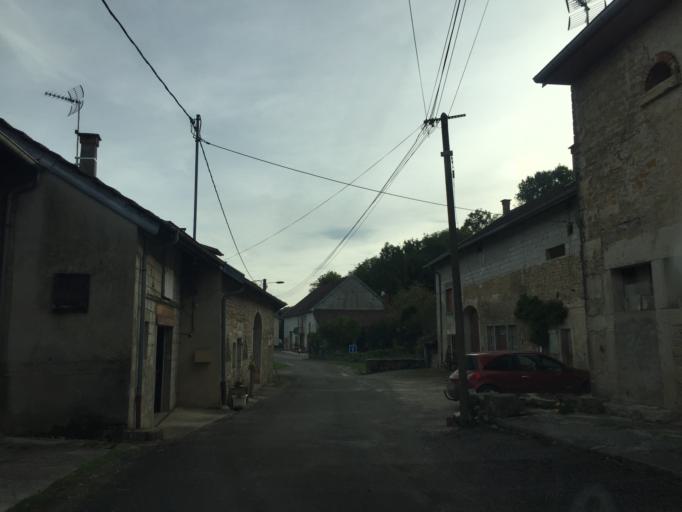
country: FR
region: Franche-Comte
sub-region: Departement du Jura
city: Orgelet
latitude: 46.5265
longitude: 5.5463
